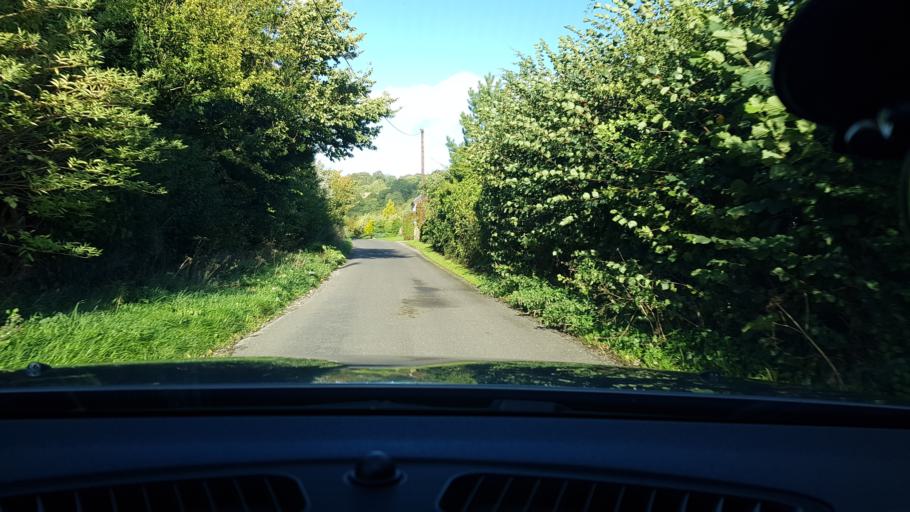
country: GB
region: England
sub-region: Wiltshire
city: Ramsbury
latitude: 51.4520
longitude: -1.5803
